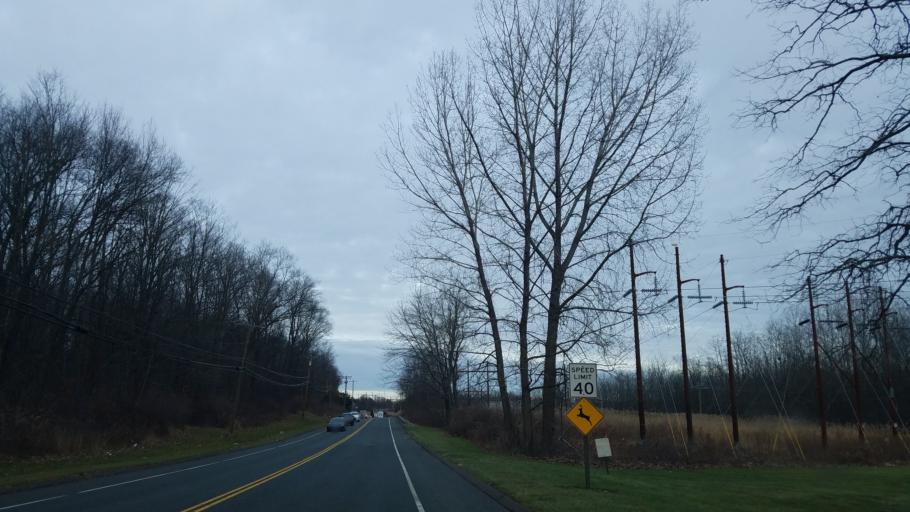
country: US
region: Connecticut
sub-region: Hartford County
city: Newington
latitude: 41.7035
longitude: -72.7528
